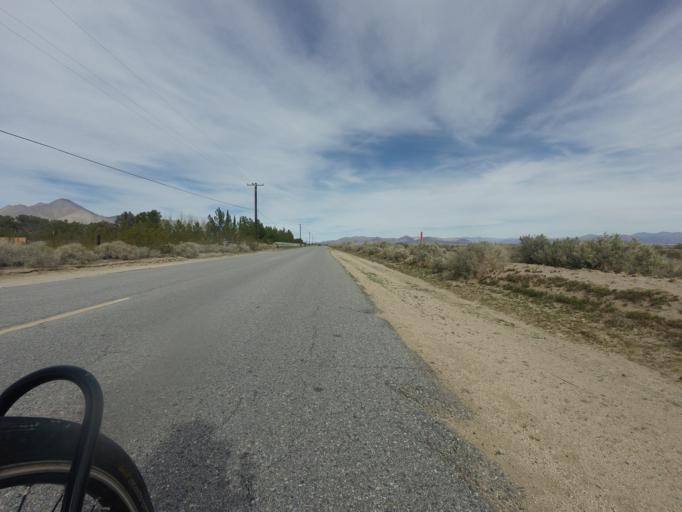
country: US
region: California
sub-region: Kern County
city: Inyokern
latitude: 35.7515
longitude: -117.8433
